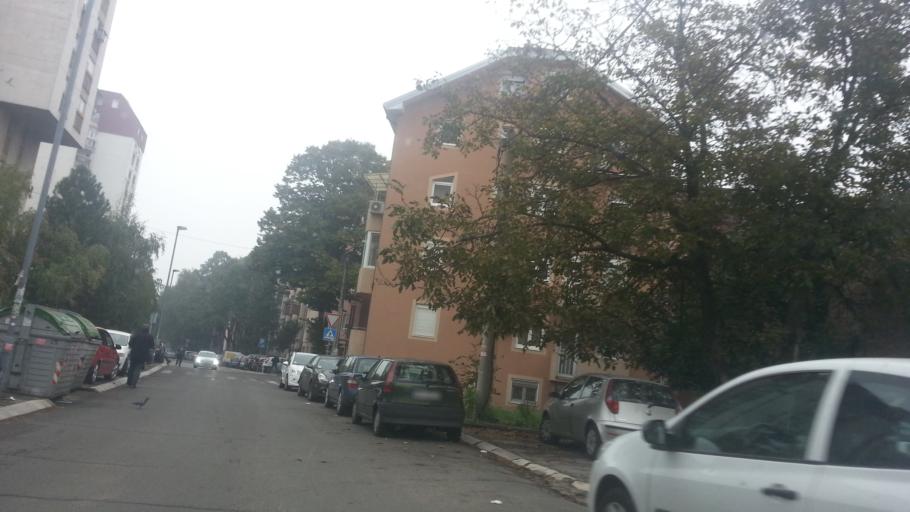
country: RS
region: Central Serbia
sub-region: Belgrade
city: Zemun
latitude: 44.8406
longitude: 20.3911
